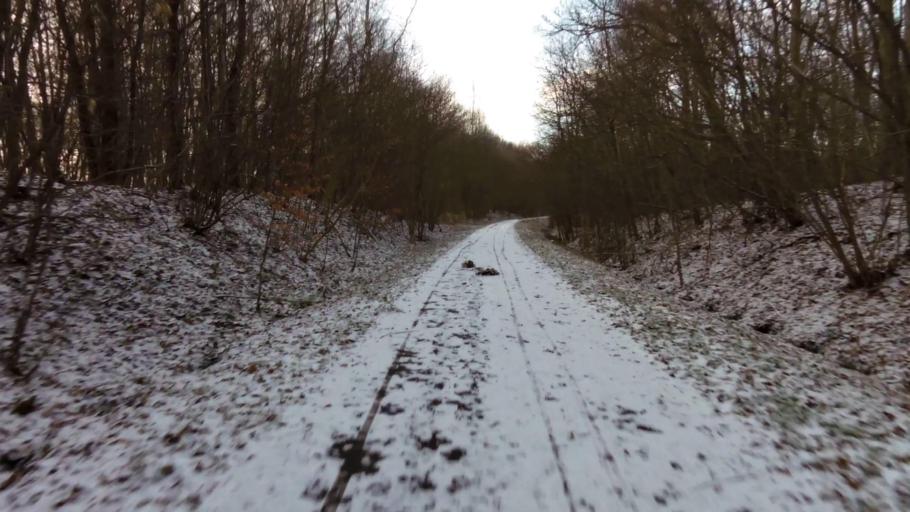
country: PL
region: West Pomeranian Voivodeship
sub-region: Powiat swidwinski
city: Polczyn-Zdroj
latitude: 53.6606
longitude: 16.0293
